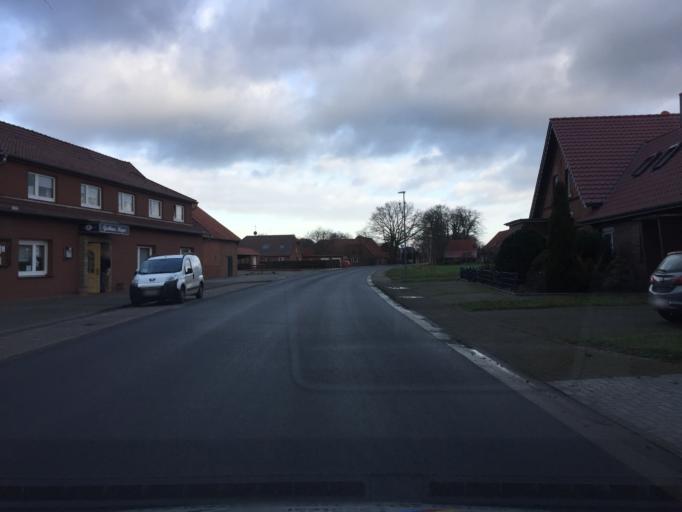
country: DE
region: Lower Saxony
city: Raddestorf
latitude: 52.5035
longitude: 8.9928
